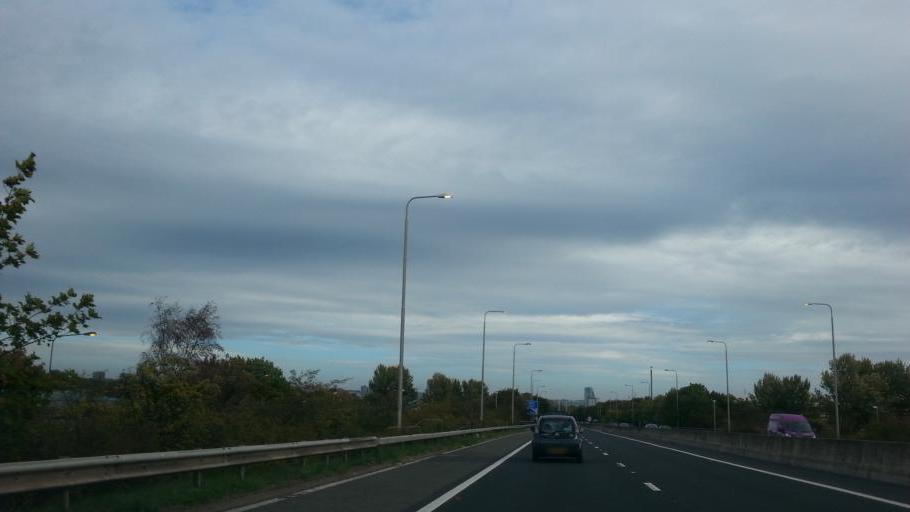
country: GB
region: England
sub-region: City and Borough of Leeds
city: Morley
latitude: 53.7742
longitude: -1.5843
